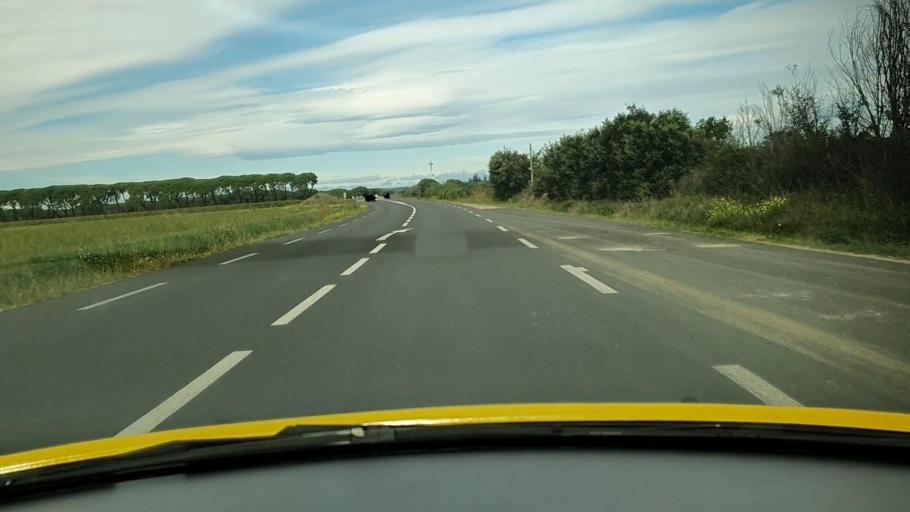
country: FR
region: Languedoc-Roussillon
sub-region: Departement du Gard
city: Garons
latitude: 43.7751
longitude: 4.4013
